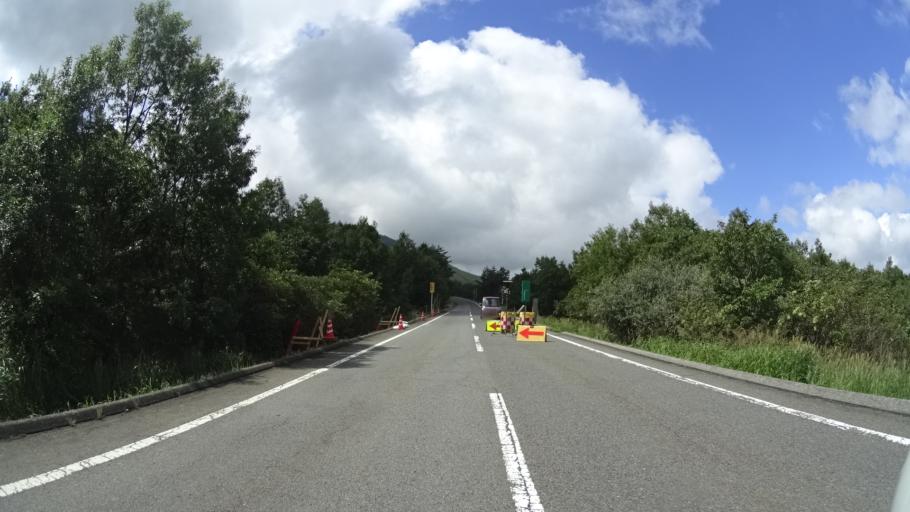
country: JP
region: Oita
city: Tsukawaki
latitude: 33.1314
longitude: 131.2309
